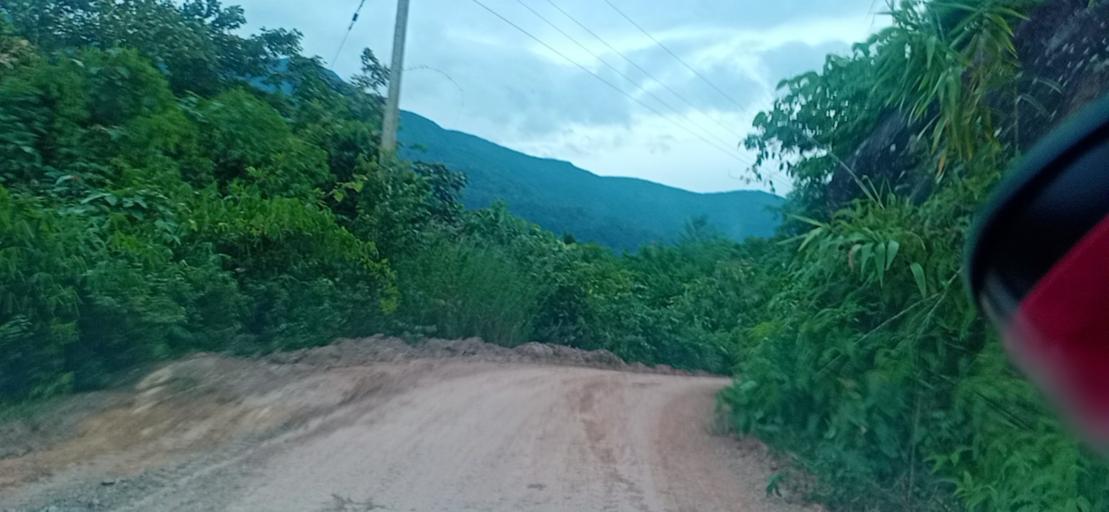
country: TH
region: Changwat Bueng Kan
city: Pak Khat
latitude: 18.5518
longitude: 103.4259
